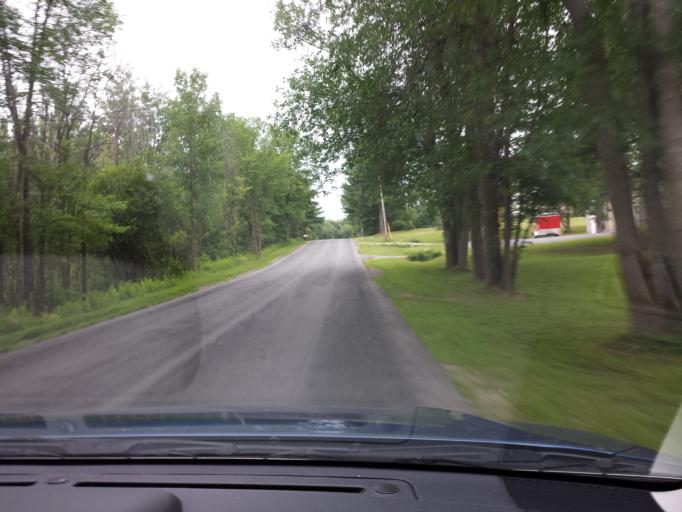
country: US
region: New York
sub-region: St. Lawrence County
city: Potsdam
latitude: 44.7048
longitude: -74.9618
